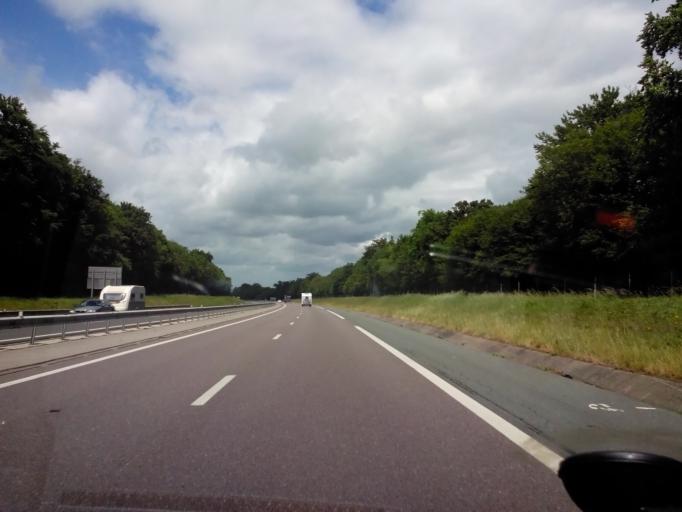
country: FR
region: Lorraine
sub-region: Departement de Meurthe-et-Moselle
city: Colombey-les-Belles
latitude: 48.5218
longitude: 5.9156
